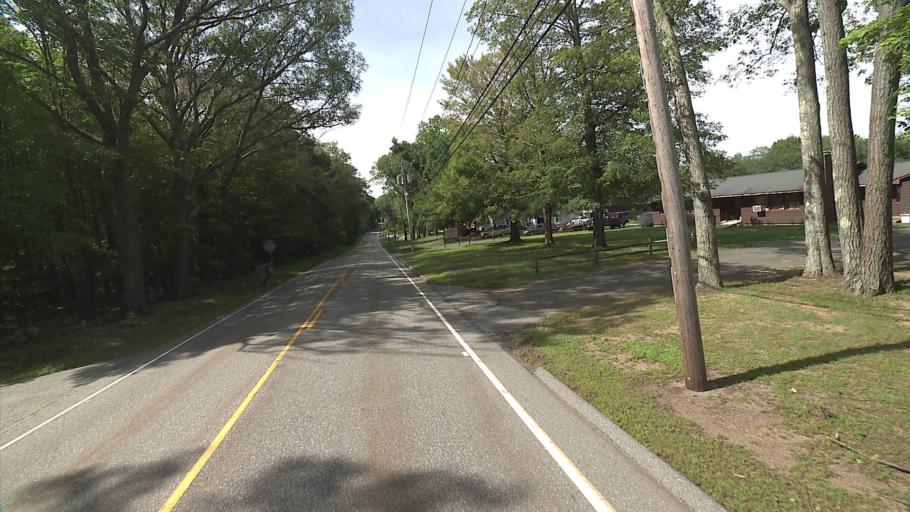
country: US
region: Massachusetts
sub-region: Hampden County
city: Holland
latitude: 41.9973
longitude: -72.1527
